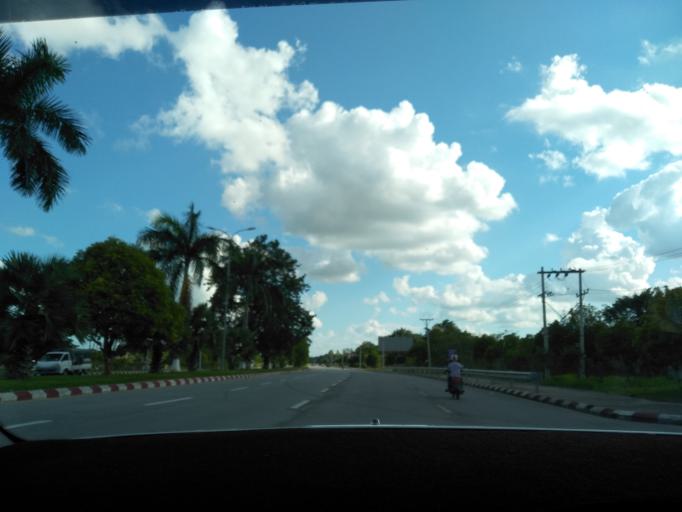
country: MM
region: Mandalay
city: Nay Pyi Taw
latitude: 19.7328
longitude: 96.1112
